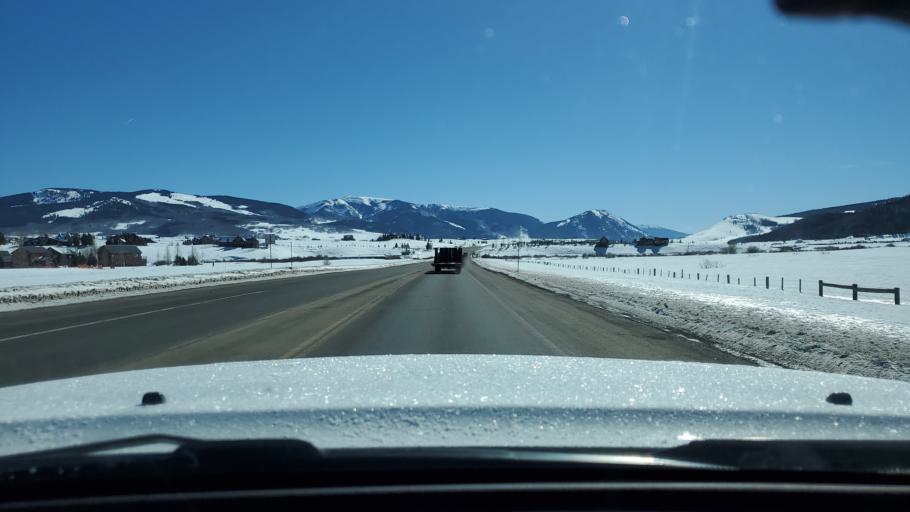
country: US
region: Colorado
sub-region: Gunnison County
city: Crested Butte
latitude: 38.8535
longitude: -106.9569
